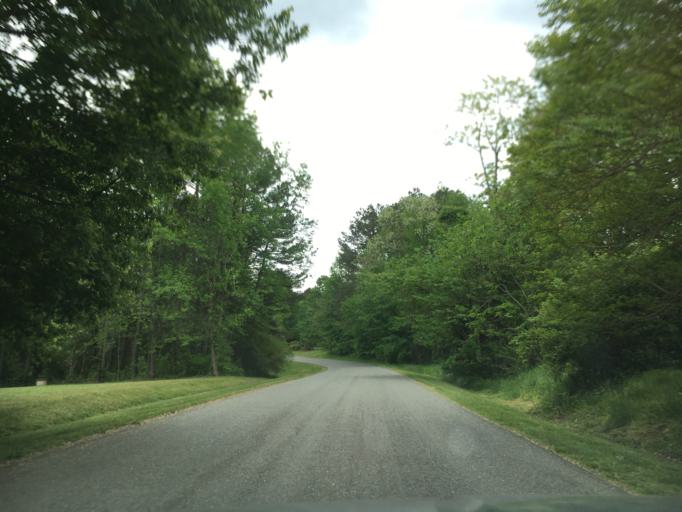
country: US
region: Virginia
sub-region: Halifax County
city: Halifax
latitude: 36.7976
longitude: -78.9397
